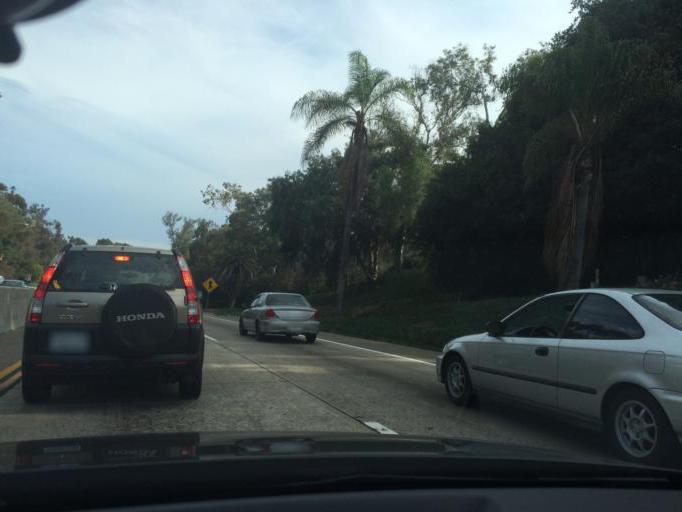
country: US
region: California
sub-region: San Diego County
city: San Diego
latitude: 32.7462
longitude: -117.1566
